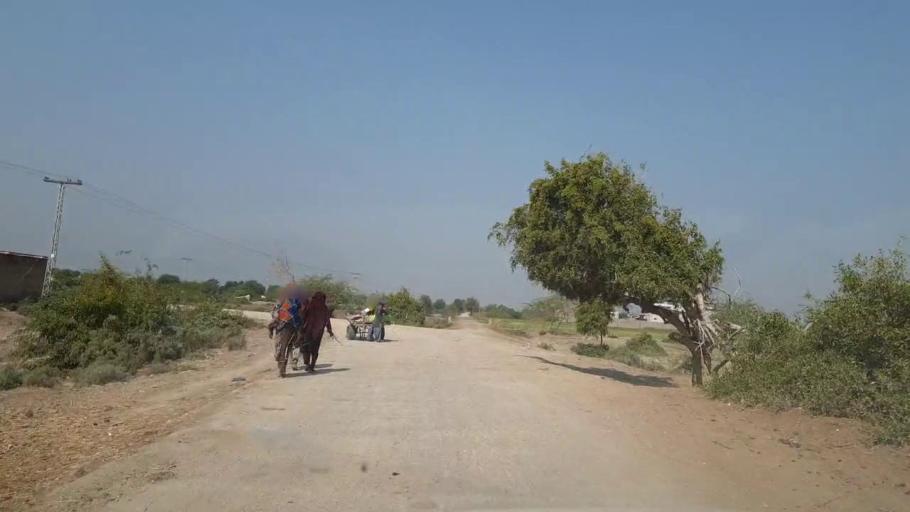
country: PK
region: Sindh
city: Mirpur Khas
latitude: 25.6294
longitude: 69.1106
